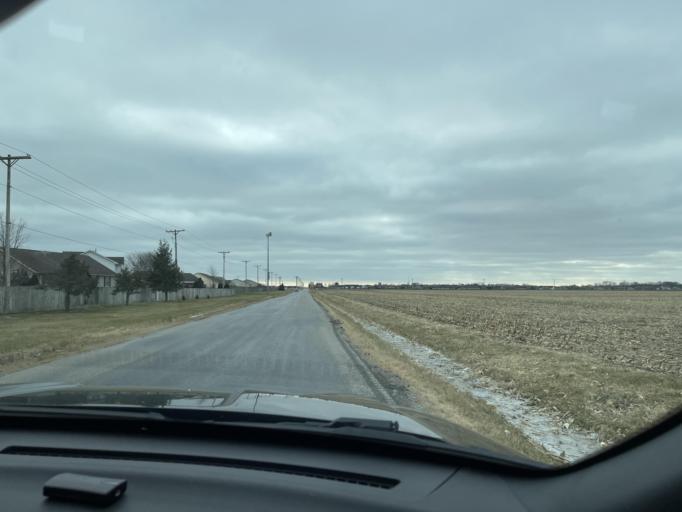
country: US
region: Illinois
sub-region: Sangamon County
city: Jerome
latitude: 39.7748
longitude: -89.7535
